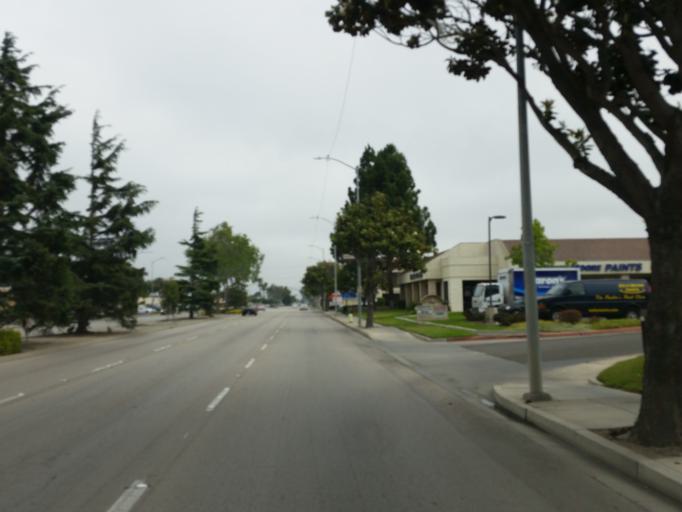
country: US
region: California
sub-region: Santa Barbara County
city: Santa Maria
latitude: 34.9277
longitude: -120.4359
